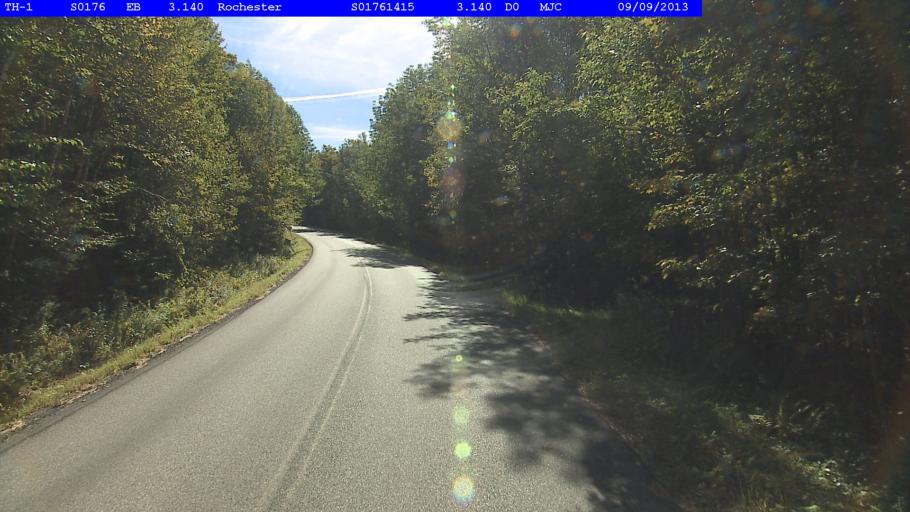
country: US
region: Vermont
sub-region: Orange County
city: Randolph
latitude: 43.8596
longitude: -72.7616
